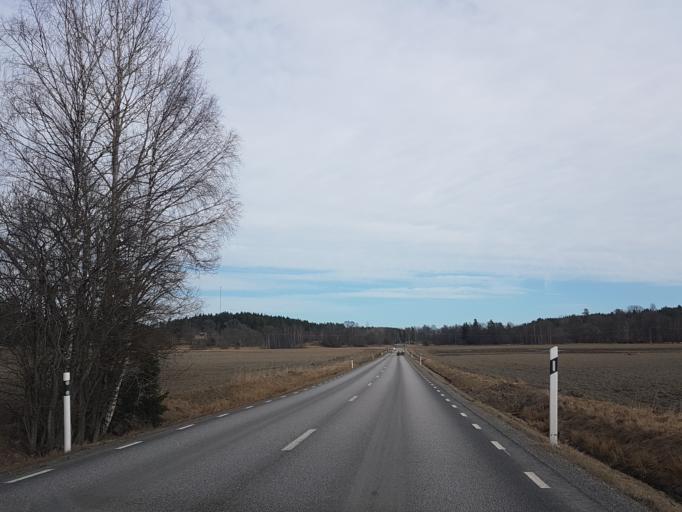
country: SE
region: Stockholm
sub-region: Norrtalje Kommun
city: Norrtalje
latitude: 59.6796
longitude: 18.6887
